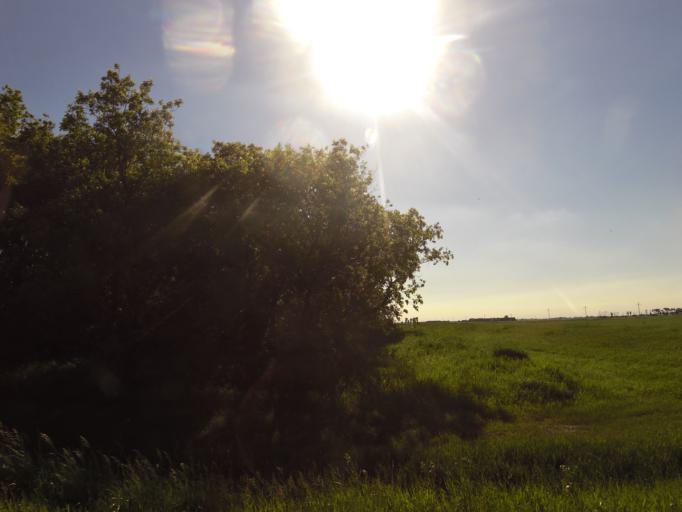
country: US
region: North Dakota
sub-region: Walsh County
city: Grafton
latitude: 48.4101
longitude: -97.2339
